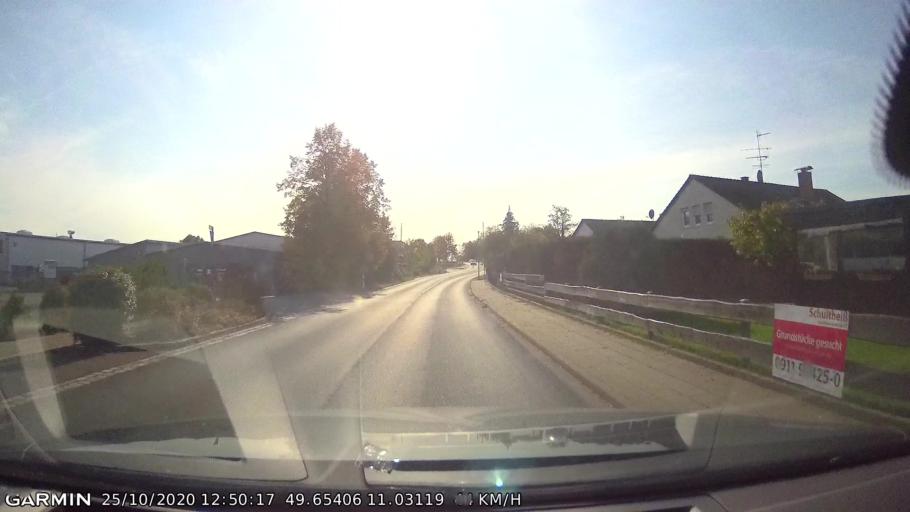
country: DE
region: Bavaria
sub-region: Regierungsbezirk Mittelfranken
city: Baiersdorf
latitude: 49.6538
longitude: 11.0311
